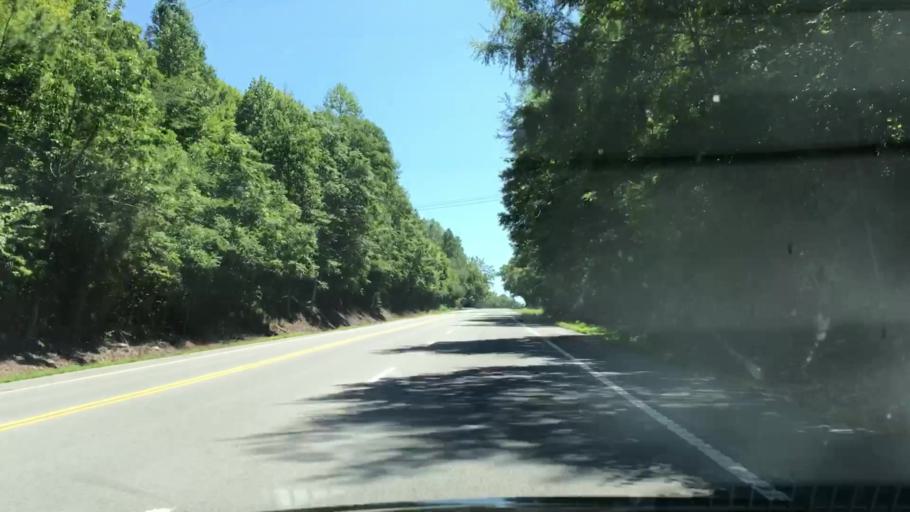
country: US
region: Tennessee
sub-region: Jackson County
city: Gainesboro
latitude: 36.3066
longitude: -85.6436
